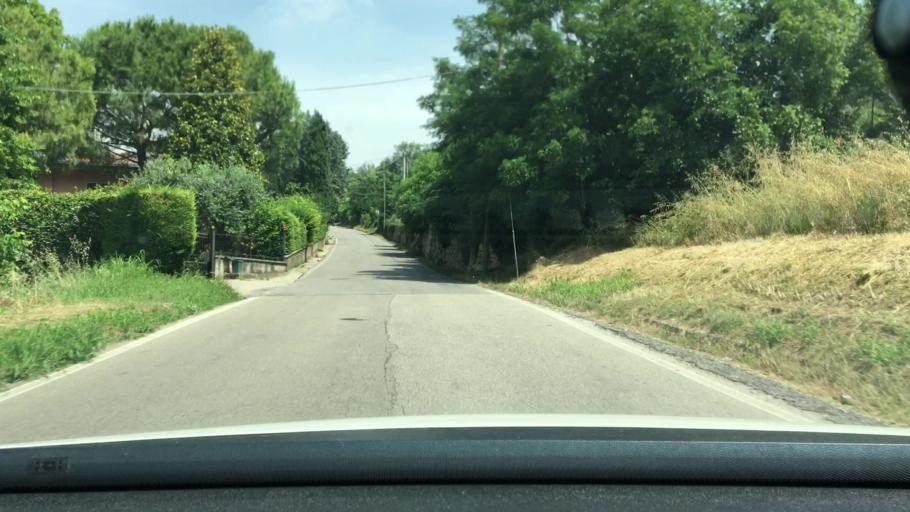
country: IT
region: Veneto
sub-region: Provincia di Verona
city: Monticelli-Fontana
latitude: 45.4275
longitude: 11.1203
